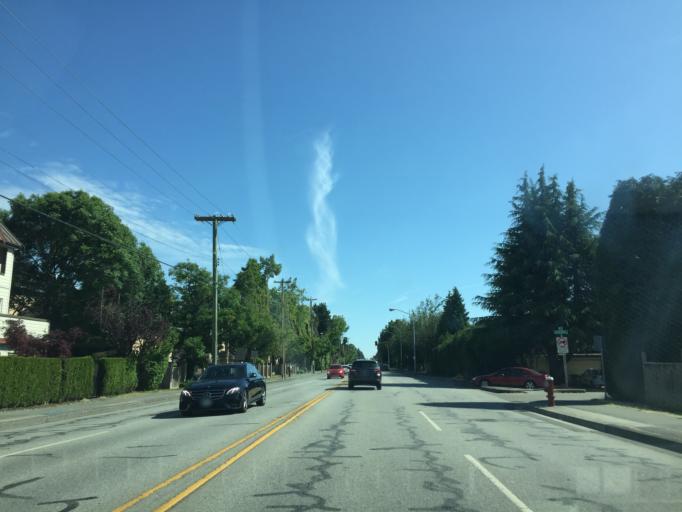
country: CA
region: British Columbia
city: Richmond
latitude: 49.1606
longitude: -123.1366
